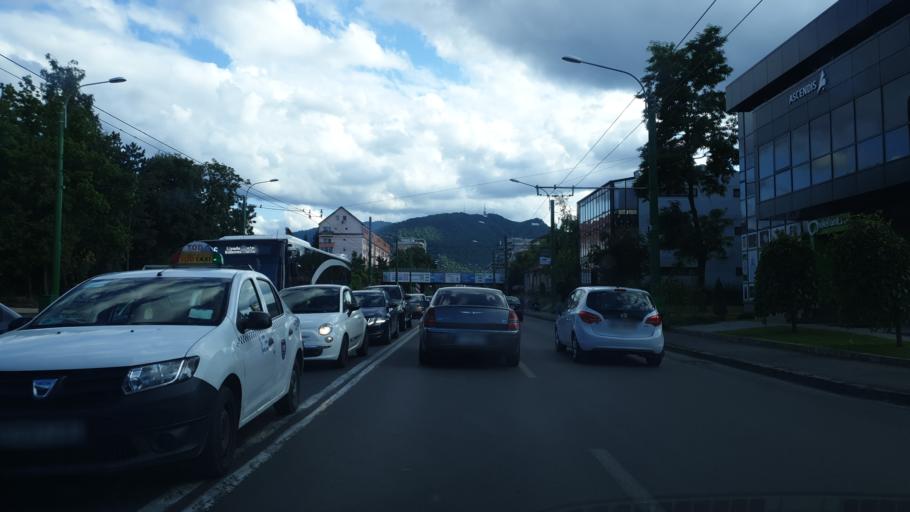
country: RO
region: Brasov
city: Brasov
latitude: 45.6637
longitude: 25.6086
